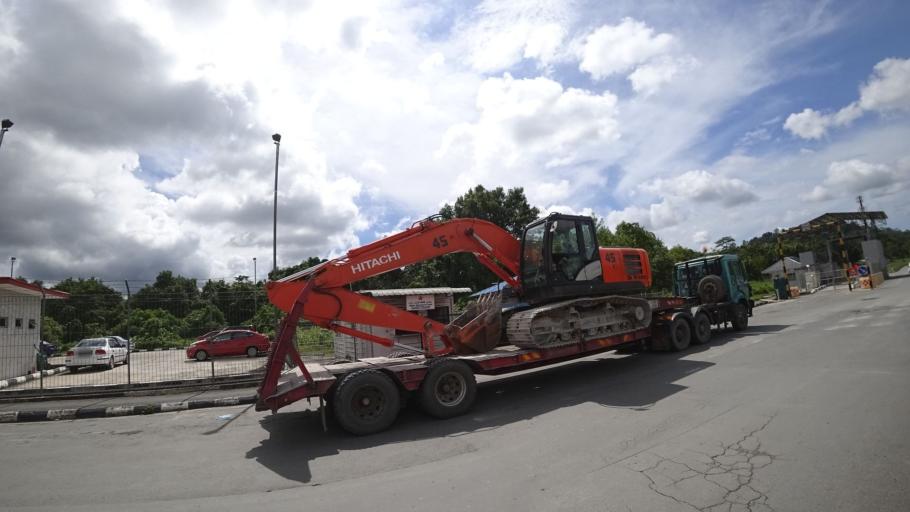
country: BN
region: Tutong
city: Tutong
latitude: 4.7411
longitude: 114.8136
